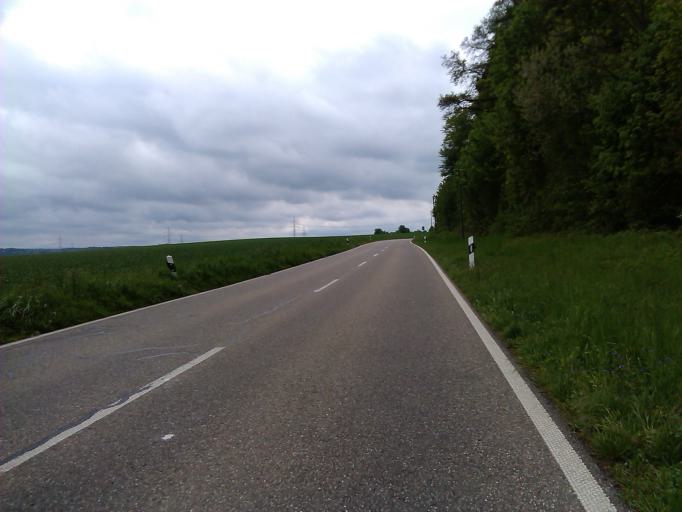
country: DE
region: Baden-Wuerttemberg
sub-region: Karlsruhe Region
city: Knittlingen
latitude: 49.0459
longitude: 8.7502
